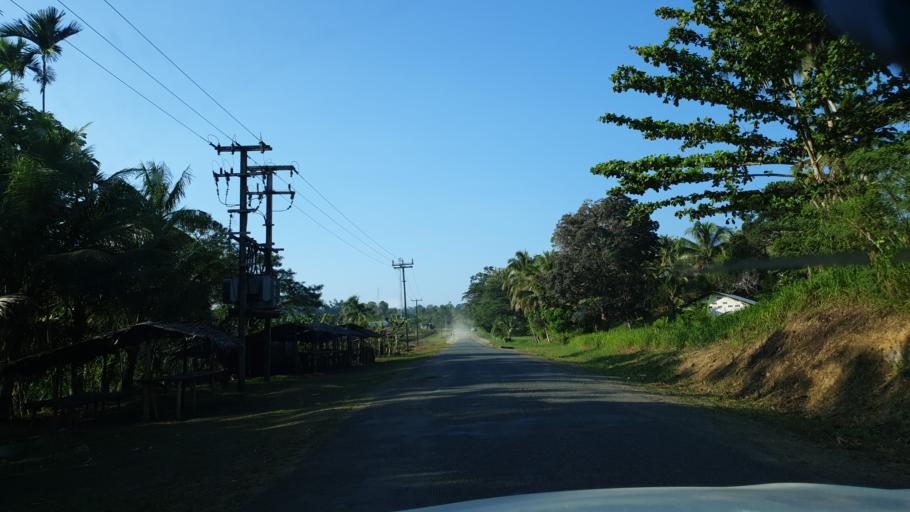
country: PG
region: East Sepik
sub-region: Wewak
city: Wewak
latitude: -3.6976
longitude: 143.6363
